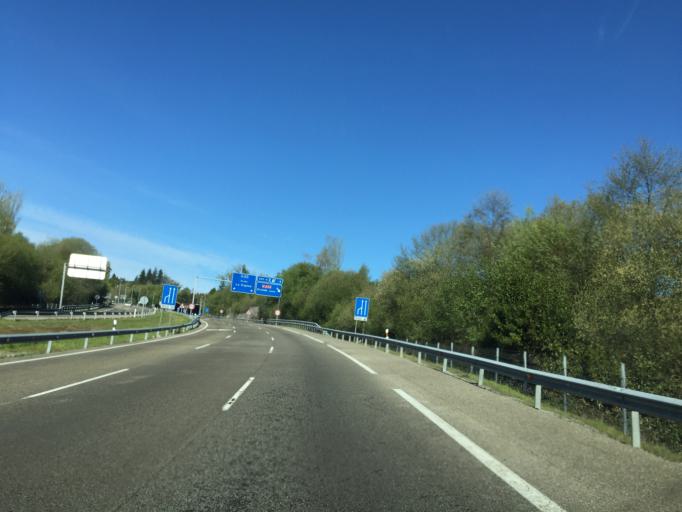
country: ES
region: Asturias
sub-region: Province of Asturias
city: Oviedo
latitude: 43.3434
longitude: -5.8861
